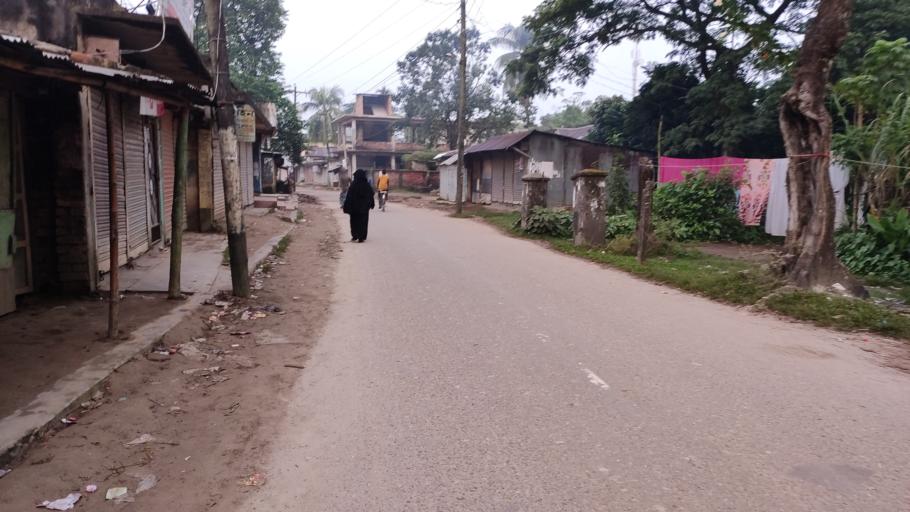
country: BD
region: Dhaka
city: Netrakona
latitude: 24.7164
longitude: 90.9570
